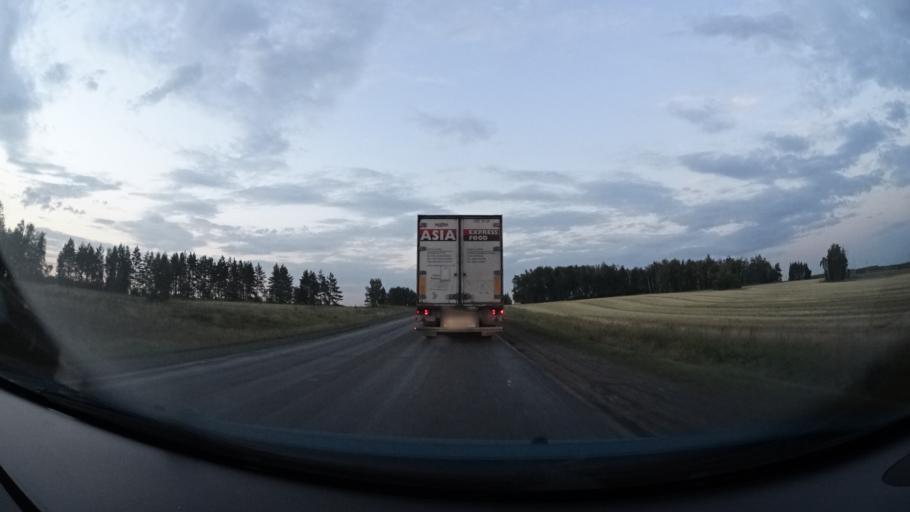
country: RU
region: Tatarstan
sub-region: Bavlinskiy Rayon
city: Bavly
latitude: 54.2867
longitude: 52.9966
